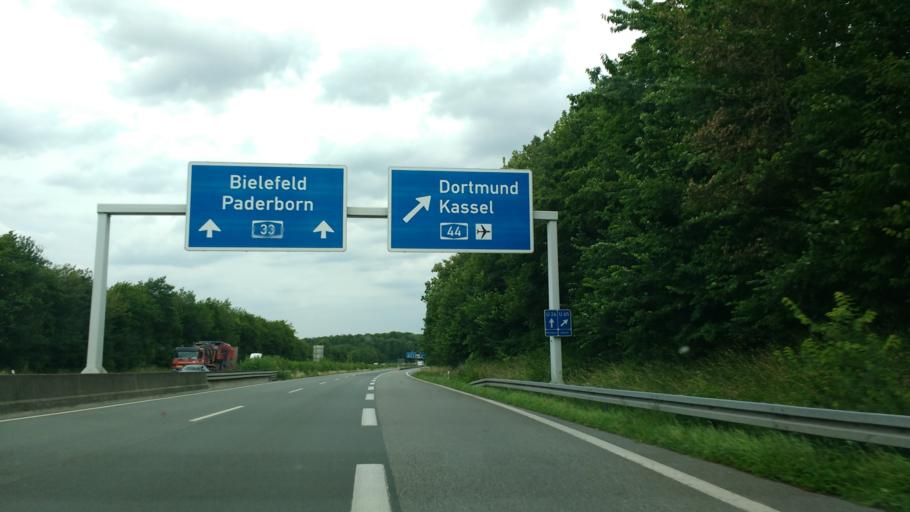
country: DE
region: North Rhine-Westphalia
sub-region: Regierungsbezirk Detmold
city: Wunnenberg
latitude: 51.5762
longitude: 8.7154
